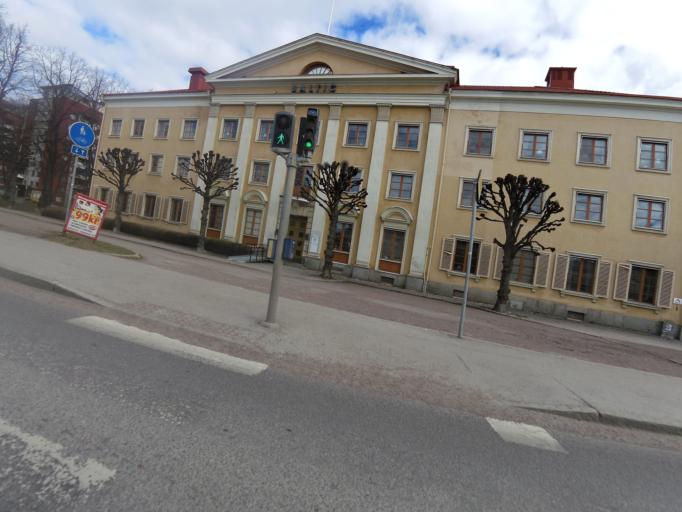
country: SE
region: Gaevleborg
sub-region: Gavle Kommun
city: Gavle
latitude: 60.6770
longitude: 17.1518
